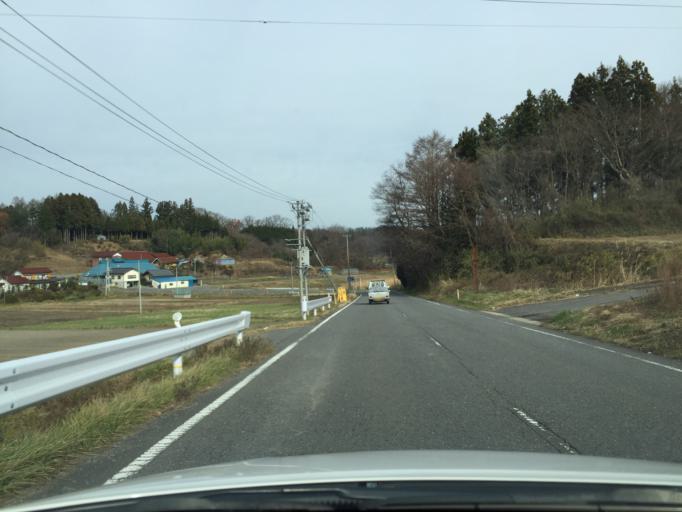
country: JP
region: Fukushima
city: Funehikimachi-funehiki
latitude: 37.4010
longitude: 140.5925
